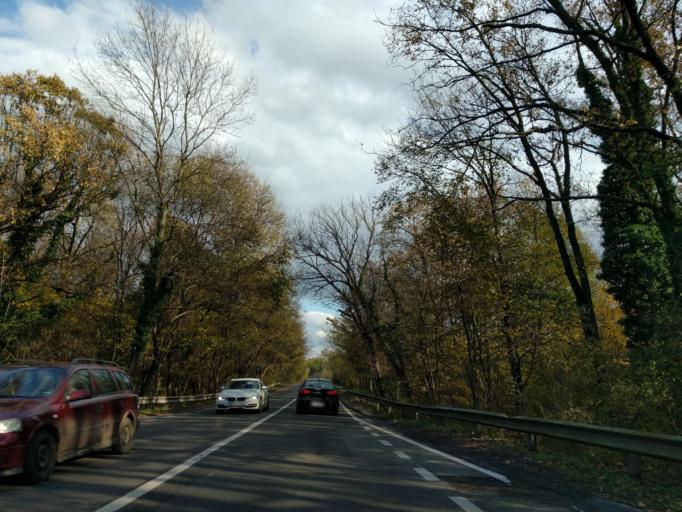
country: RO
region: Ilfov
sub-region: Comuna Branesti
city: Branesti
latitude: 44.4615
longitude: 26.3186
